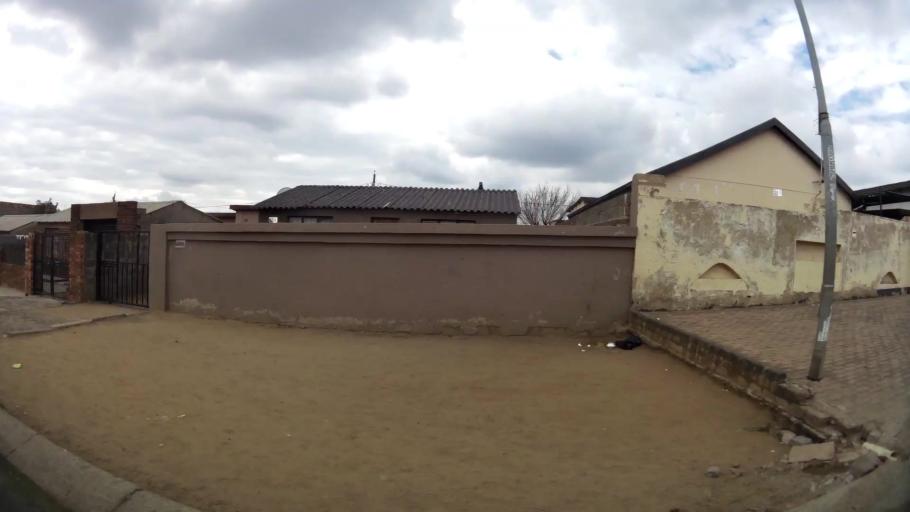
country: ZA
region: Gauteng
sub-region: City of Johannesburg Metropolitan Municipality
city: Soweto
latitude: -26.2695
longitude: 27.8650
